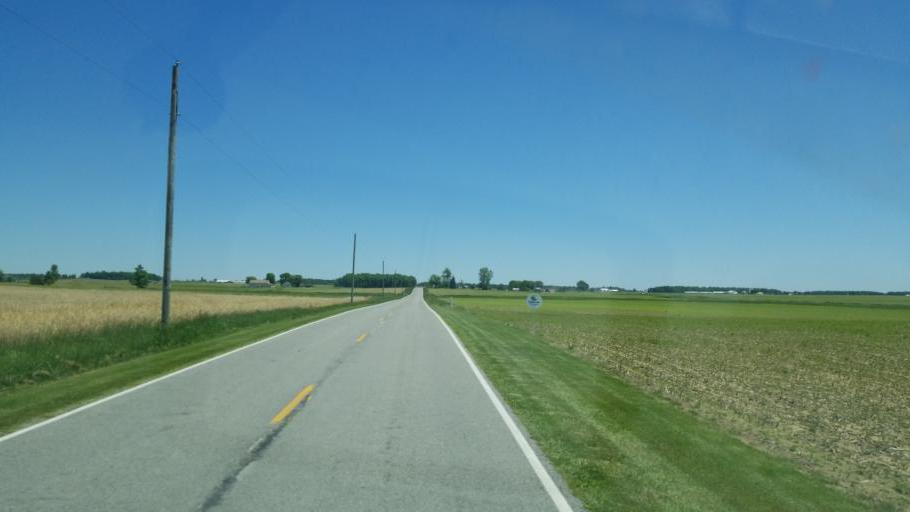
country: US
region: Ohio
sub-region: Darke County
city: Ansonia
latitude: 40.2796
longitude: -84.7202
